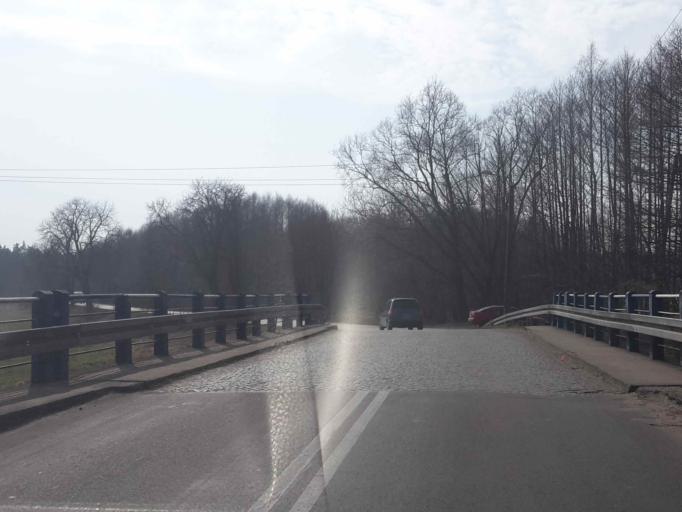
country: PL
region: Kujawsko-Pomorskie
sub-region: Powiat nakielski
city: Szubin
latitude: 53.0828
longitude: 17.7318
